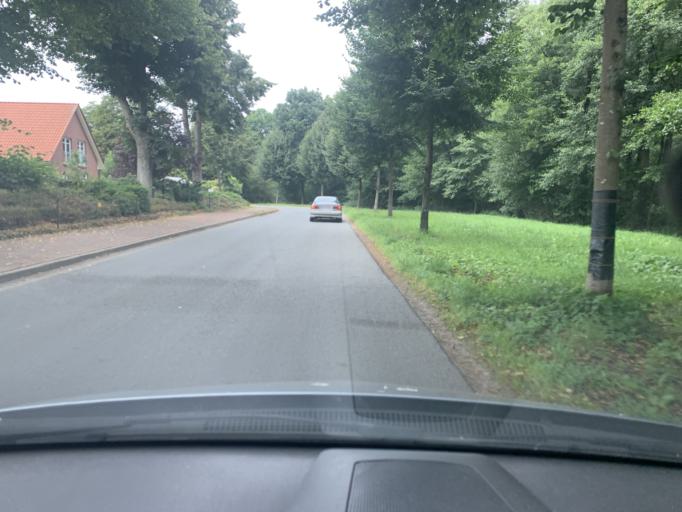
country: DE
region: Schleswig-Holstein
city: Grambek
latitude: 53.5704
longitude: 10.6841
